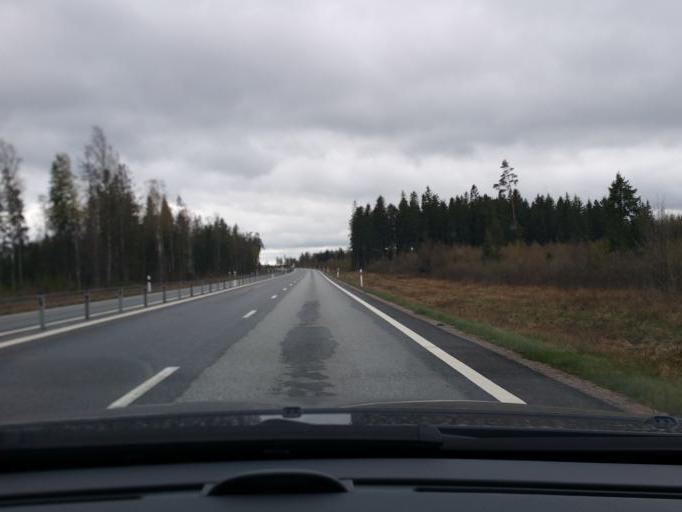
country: SE
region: Kronoberg
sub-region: Vaxjo Kommun
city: Vaexjoe
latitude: 56.9315
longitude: 14.7215
